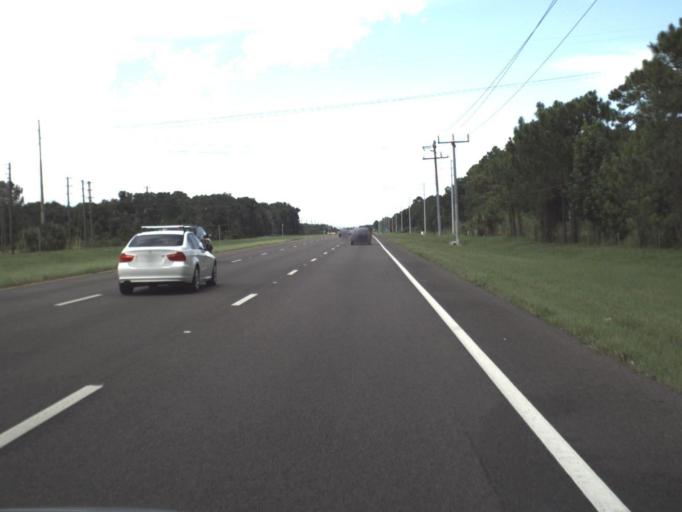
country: US
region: Florida
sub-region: Pasco County
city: Wesley Chapel
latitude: 28.1990
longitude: -82.3533
